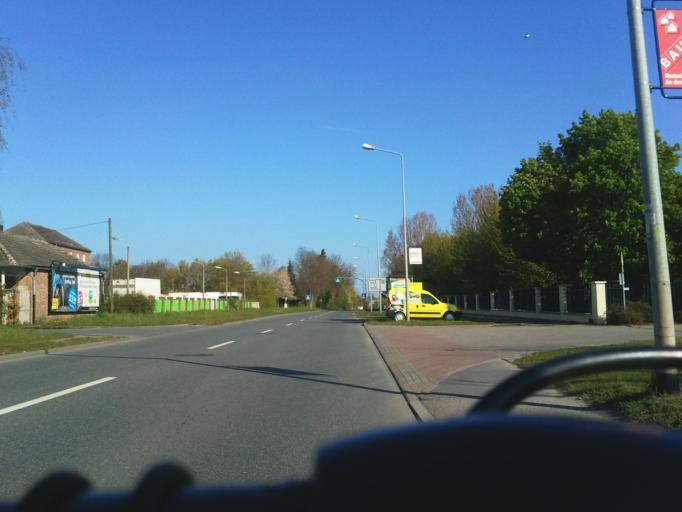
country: DE
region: Mecklenburg-Vorpommern
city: Rostock
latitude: 54.1006
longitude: 12.0947
